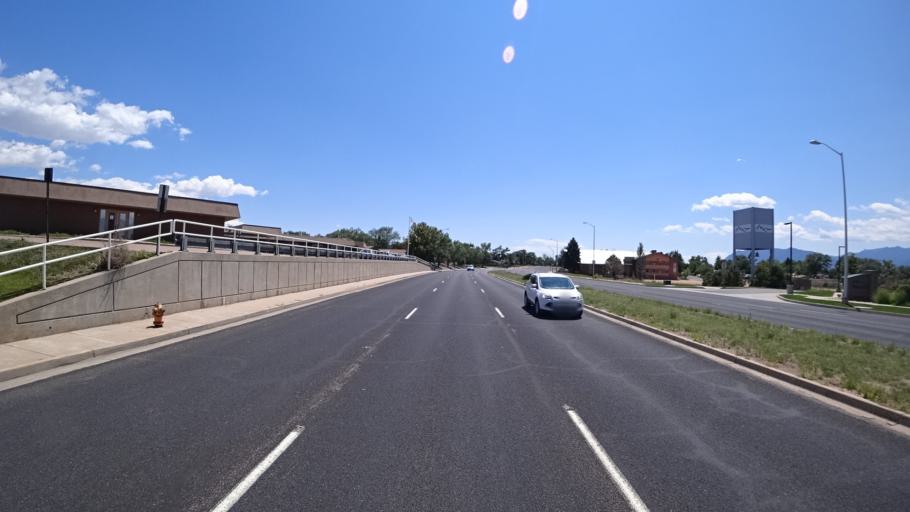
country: US
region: Colorado
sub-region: El Paso County
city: Colorado Springs
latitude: 38.8719
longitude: -104.7946
